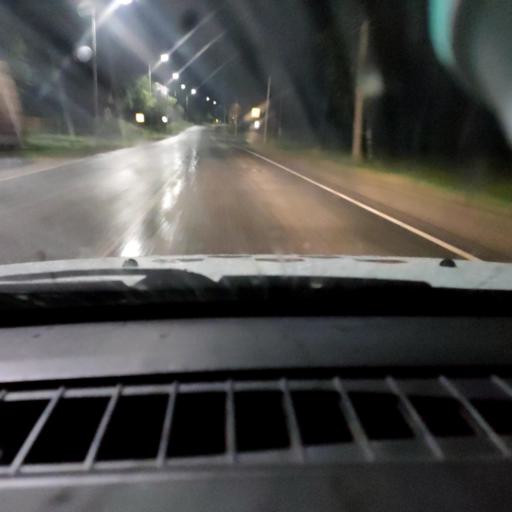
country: RU
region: Udmurtiya
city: Igra
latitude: 57.3301
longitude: 53.1668
